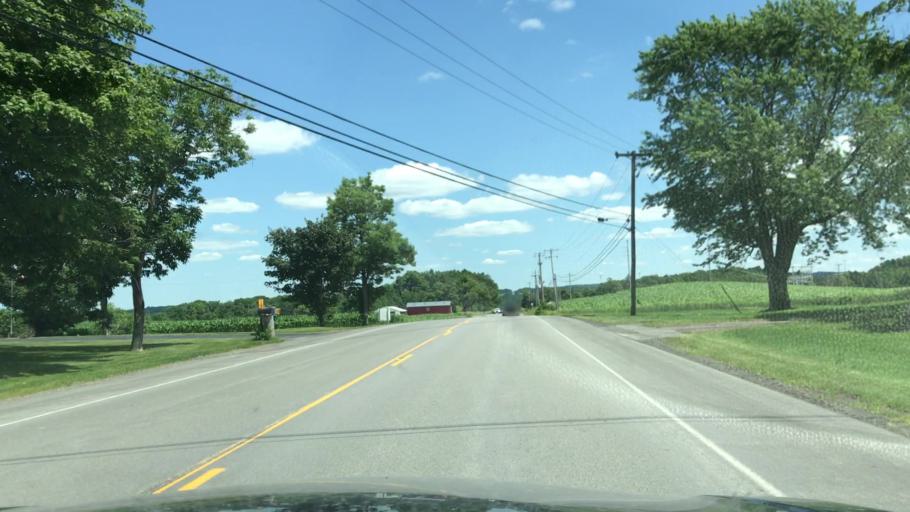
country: US
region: New York
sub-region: Erie County
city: Alden
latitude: 42.7701
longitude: -78.4071
